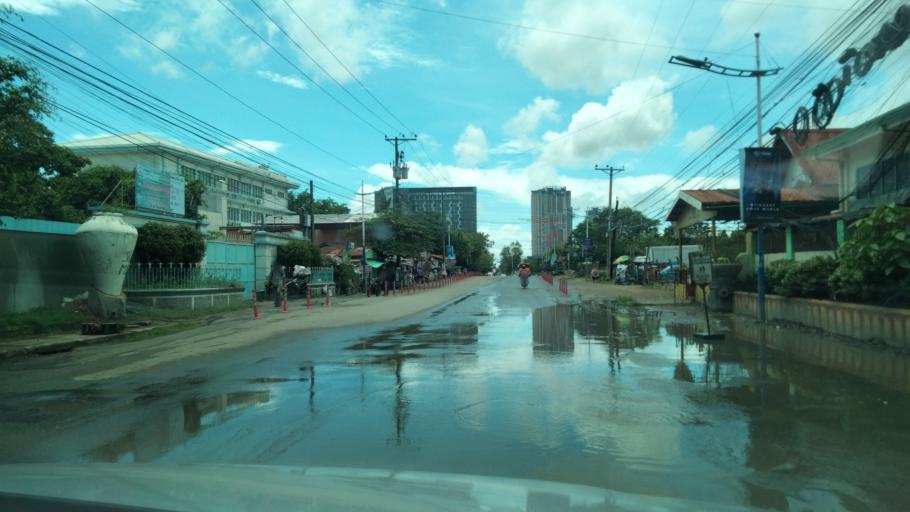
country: PH
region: Central Visayas
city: Mandaue City
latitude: 10.3284
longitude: 123.9334
